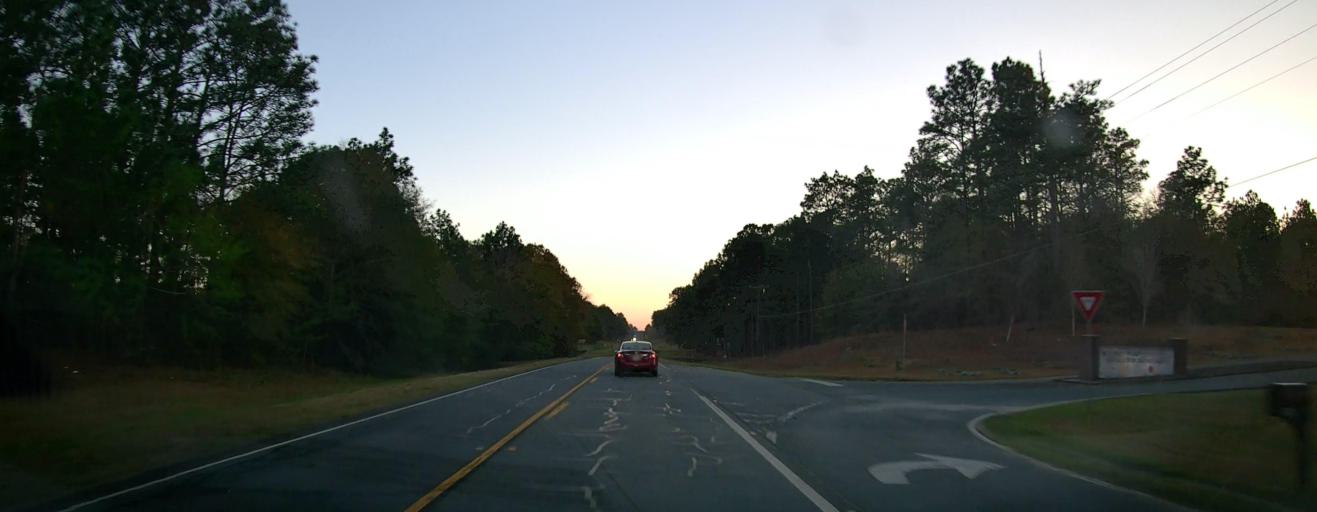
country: US
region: Georgia
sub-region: Dodge County
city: Eastman
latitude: 32.2224
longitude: -83.1559
